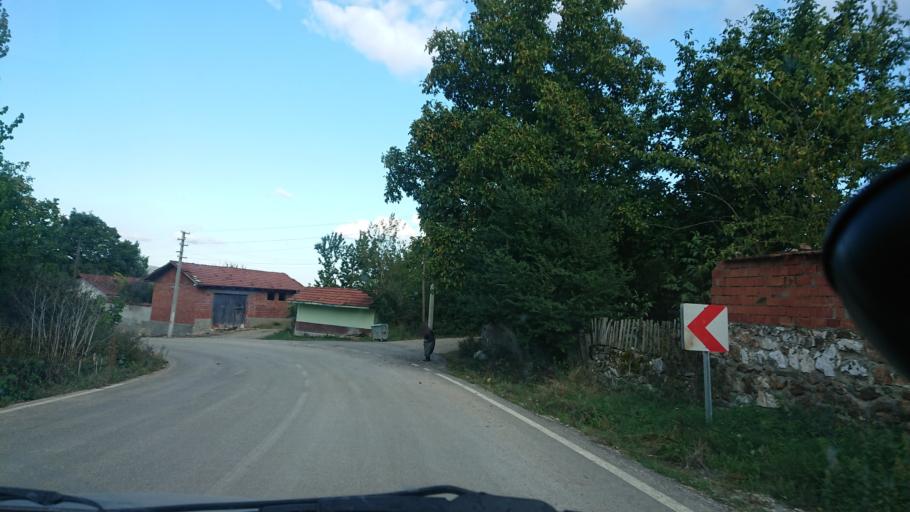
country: TR
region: Bilecik
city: Pazaryeri
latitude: 40.0103
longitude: 29.7992
